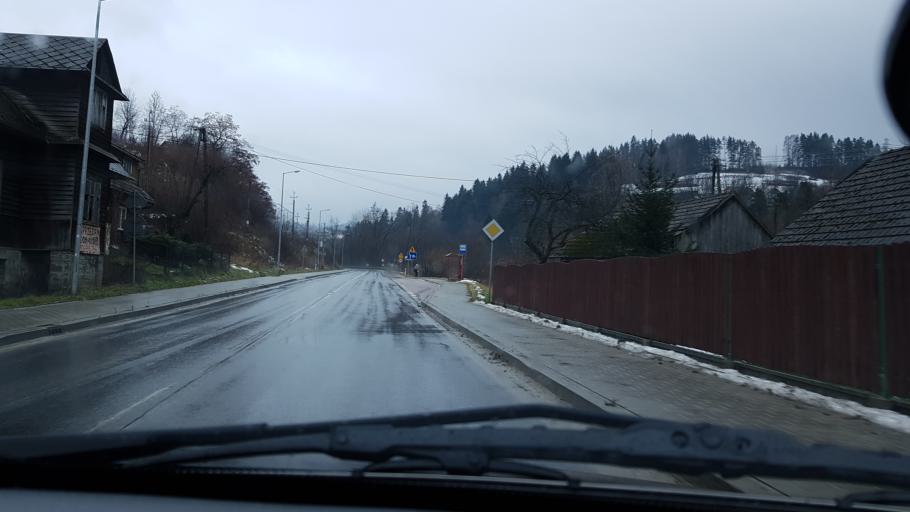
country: PL
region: Lesser Poland Voivodeship
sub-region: Powiat nowotarski
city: Raba Wyzna
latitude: 49.5492
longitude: 19.8835
